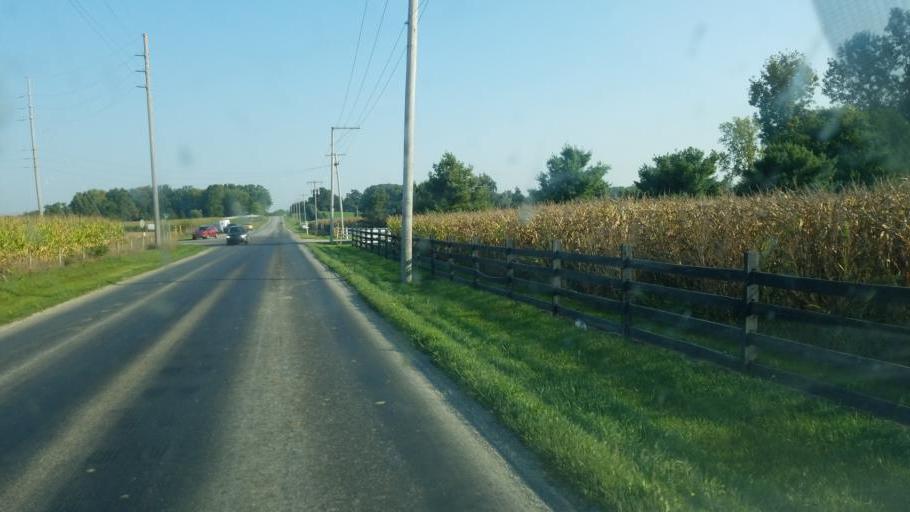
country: US
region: Indiana
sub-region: LaGrange County
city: Topeka
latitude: 41.6758
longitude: -85.5563
